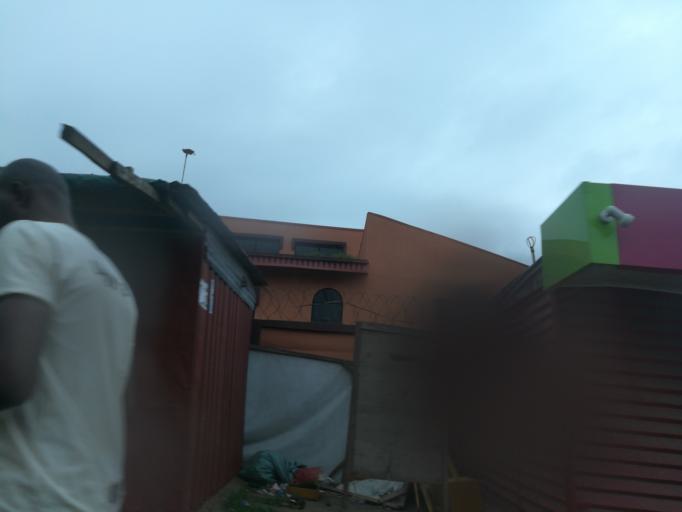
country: NG
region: Lagos
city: Oshodi
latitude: 6.5620
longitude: 3.3419
